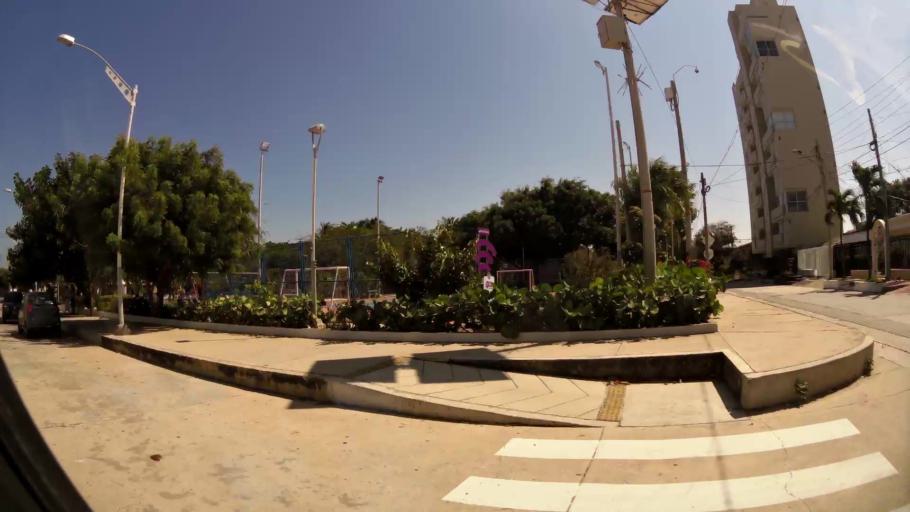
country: CO
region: Atlantico
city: Barranquilla
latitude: 11.0148
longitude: -74.8080
